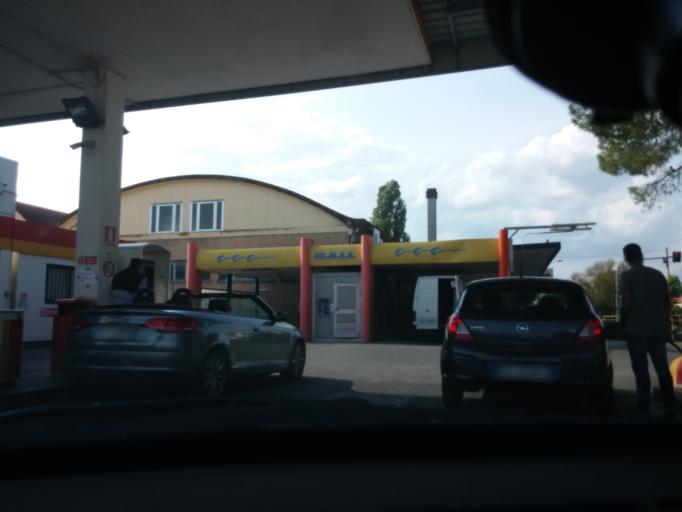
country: IT
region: Emilia-Romagna
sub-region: Provincia di Ferrara
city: Ferrara
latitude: 44.8471
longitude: 11.6007
